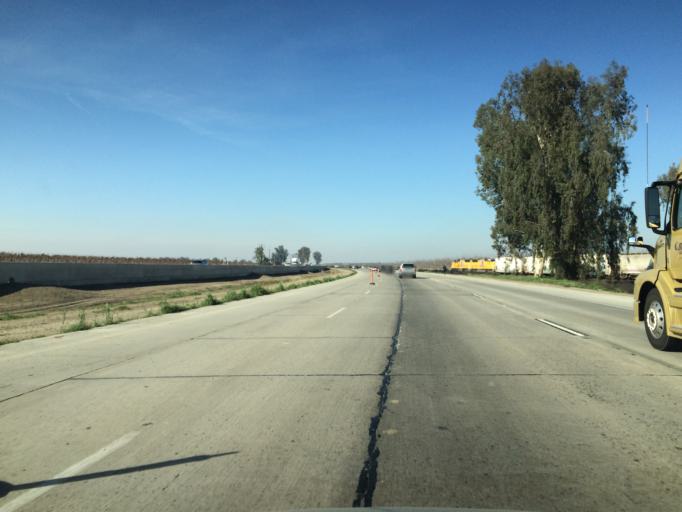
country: US
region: California
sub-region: Tulare County
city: Goshen
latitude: 36.3622
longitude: -119.4290
